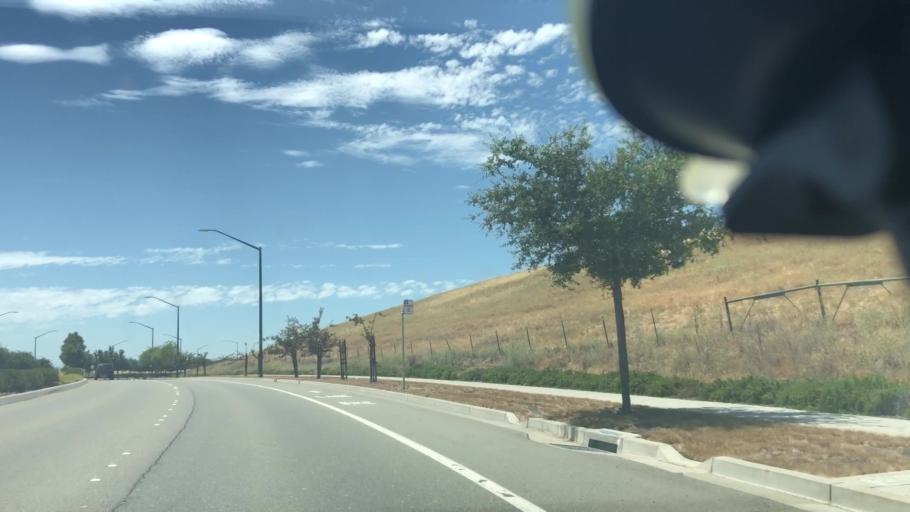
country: US
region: California
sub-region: Alameda County
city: Dublin
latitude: 37.7452
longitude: -121.8804
